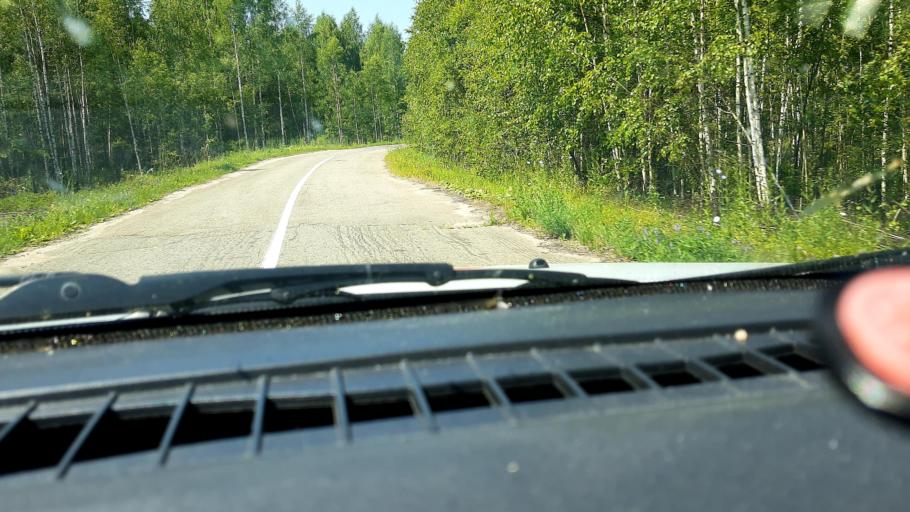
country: RU
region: Nizjnij Novgorod
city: Sharanga
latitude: 57.0615
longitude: 46.6912
